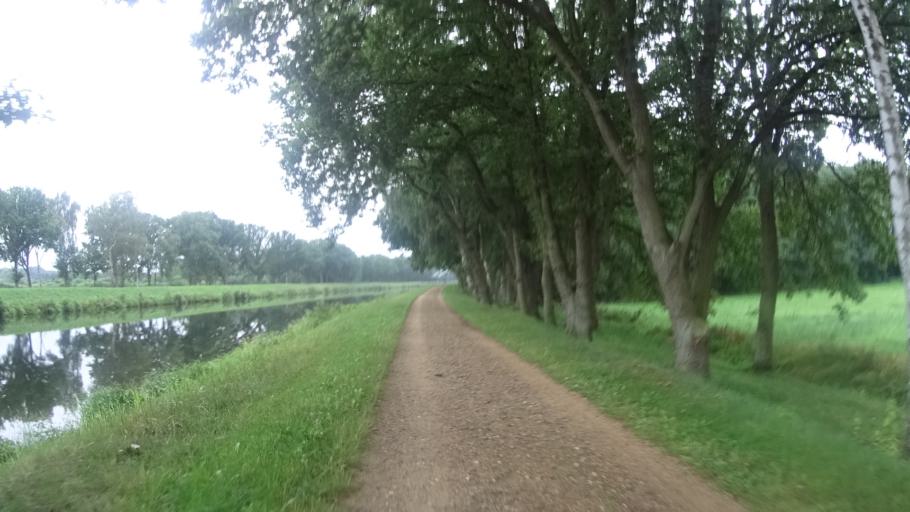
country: DE
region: Schleswig-Holstein
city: Buchen
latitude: 53.4764
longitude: 10.6313
